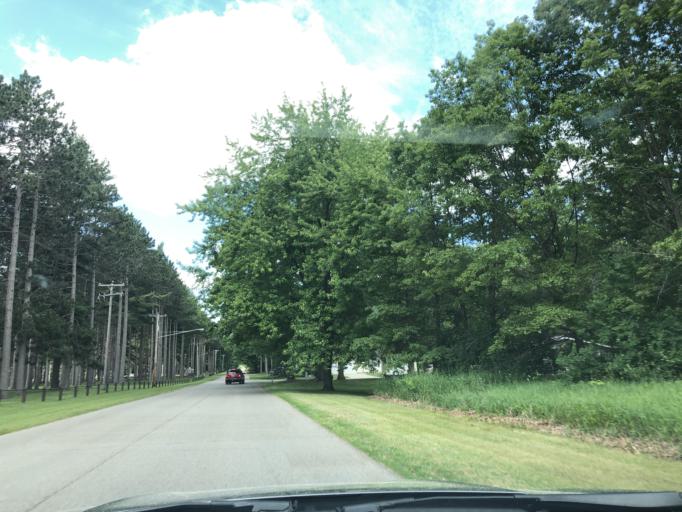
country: US
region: Michigan
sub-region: Clare County
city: Harrison
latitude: 44.0169
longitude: -84.8134
